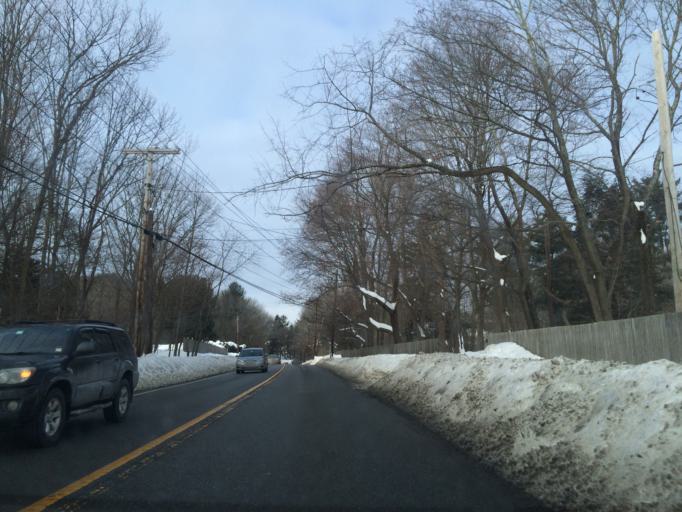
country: US
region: Massachusetts
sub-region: Middlesex County
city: Weston
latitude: 42.3648
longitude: -71.3194
